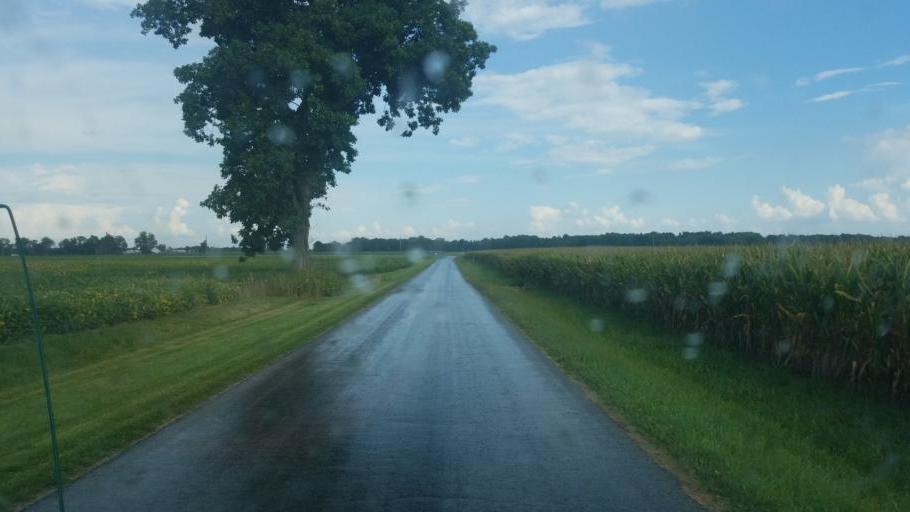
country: US
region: Ohio
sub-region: Huron County
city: Greenwich
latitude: 41.0095
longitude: -82.5632
